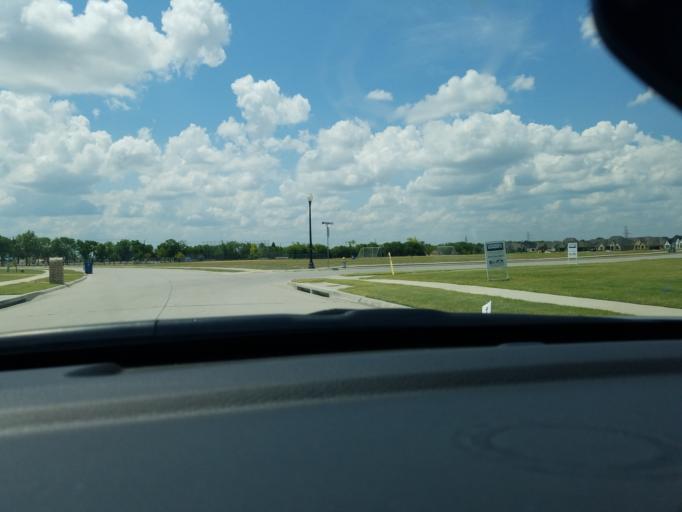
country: US
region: Texas
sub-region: Dallas County
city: Sunnyvale
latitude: 32.8121
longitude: -96.5735
